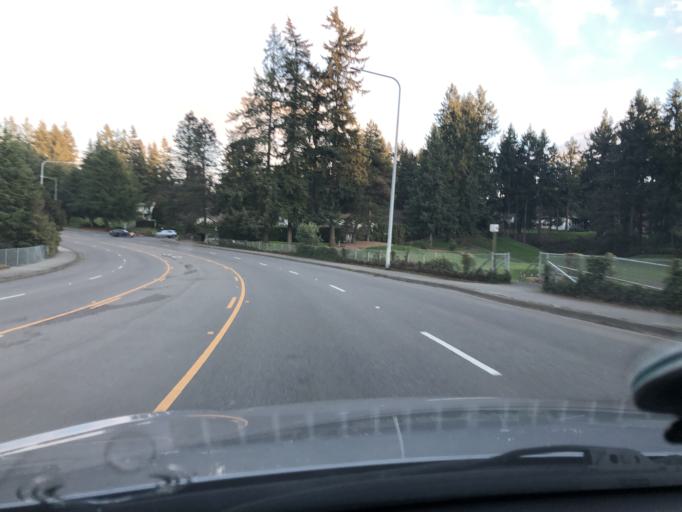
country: US
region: Washington
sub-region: Pierce County
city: Fife Heights
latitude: 47.3132
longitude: -122.3777
